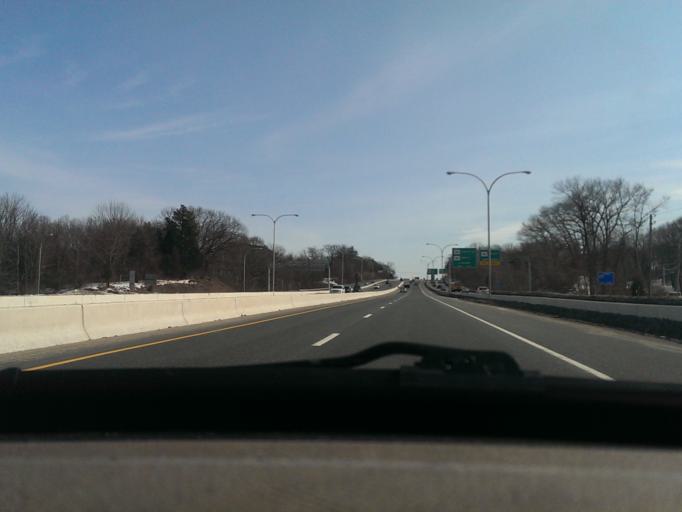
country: US
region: Rhode Island
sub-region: Providence County
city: Cumberland Hill
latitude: 41.9413
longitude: -71.4739
